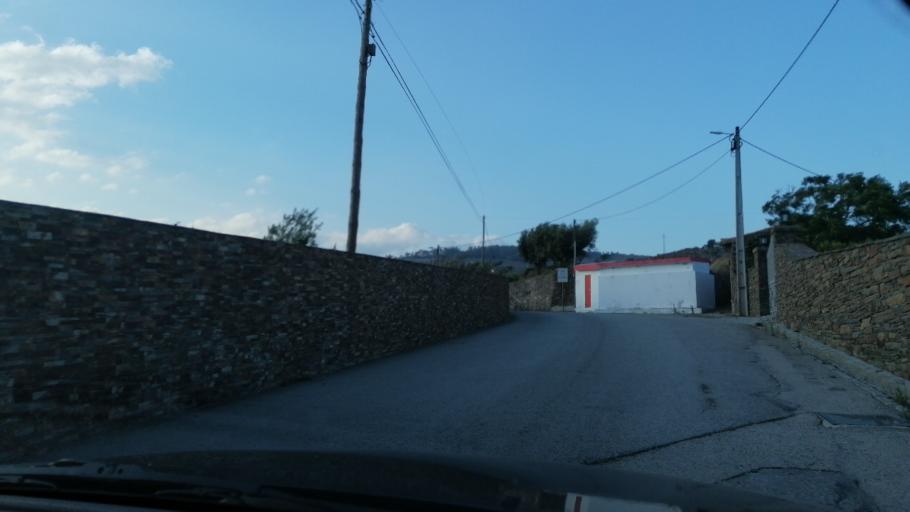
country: PT
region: Vila Real
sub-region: Peso da Regua
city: Godim
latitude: 41.1530
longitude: -7.8156
